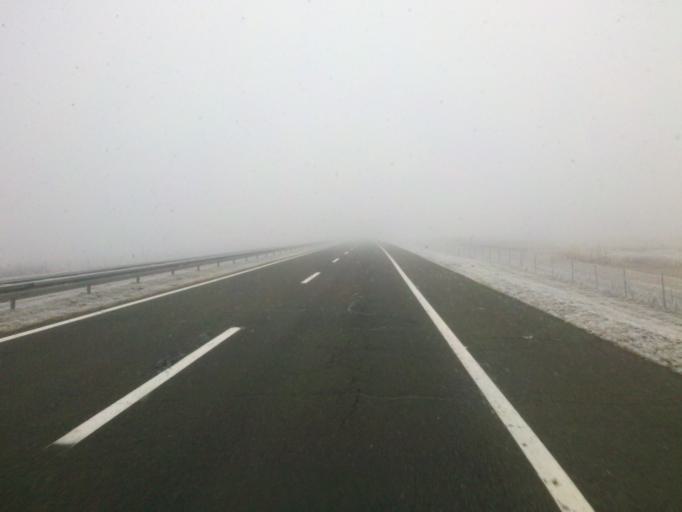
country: HR
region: Medimurska
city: Orehovica
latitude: 46.3368
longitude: 16.5271
